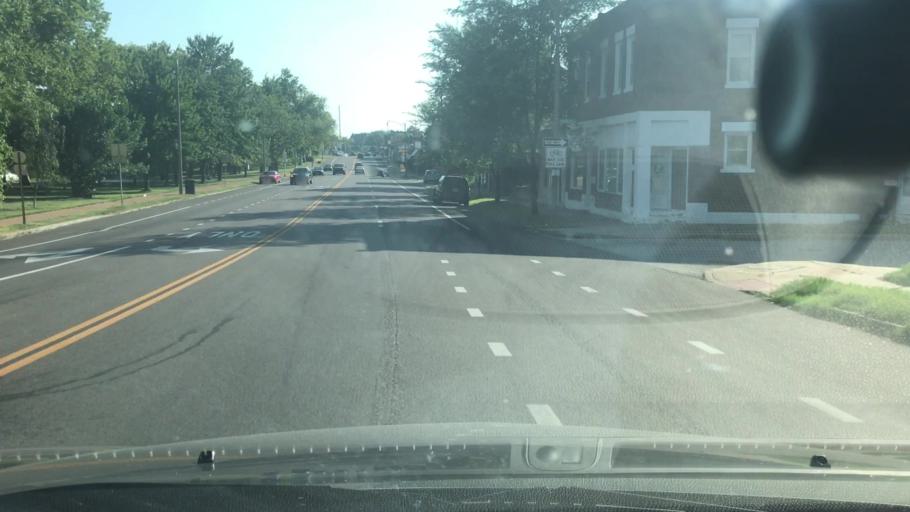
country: US
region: Missouri
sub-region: Saint Louis County
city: Lemay
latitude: 38.5766
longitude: -90.2761
